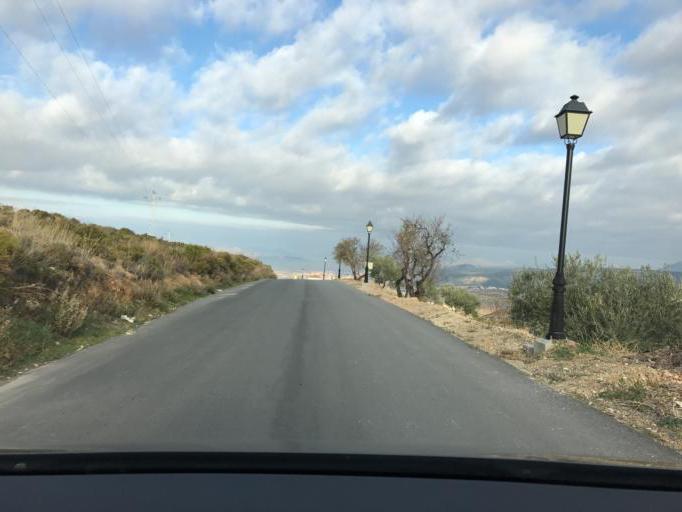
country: ES
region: Andalusia
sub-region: Provincia de Granada
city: Monachil
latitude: 37.1238
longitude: -3.5473
